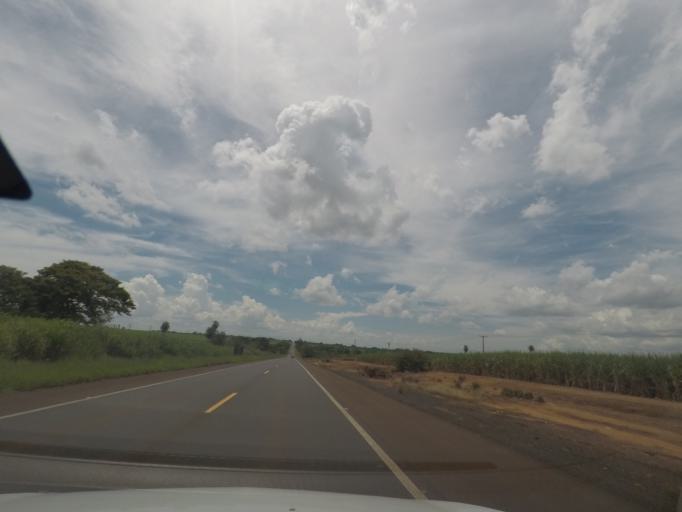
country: BR
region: Sao Paulo
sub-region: Barretos
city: Barretos
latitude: -20.3734
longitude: -48.6448
